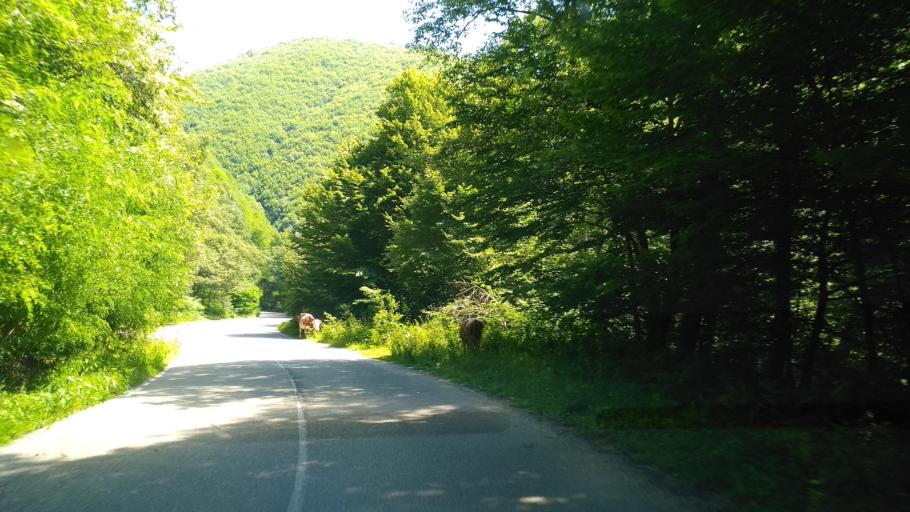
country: RO
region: Hunedoara
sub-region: Comuna Orastioara de Sus
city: Orastioara de Sus
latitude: 45.6436
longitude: 23.1958
